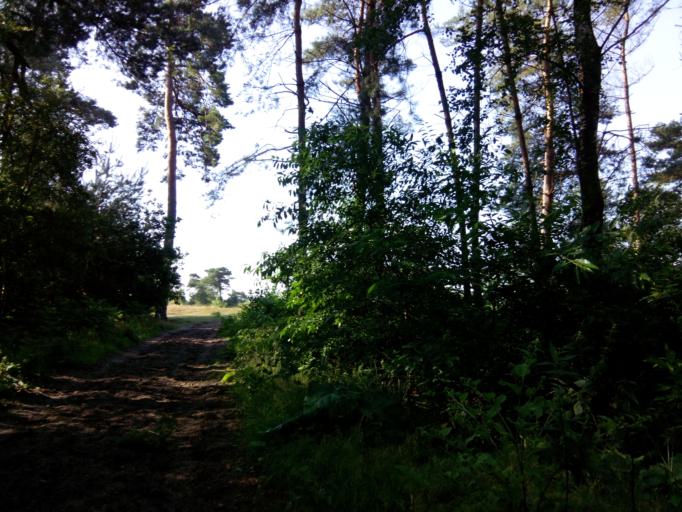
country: NL
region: Utrecht
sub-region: Gemeente Utrechtse Heuvelrug
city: Maarn
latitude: 52.1030
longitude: 5.3652
